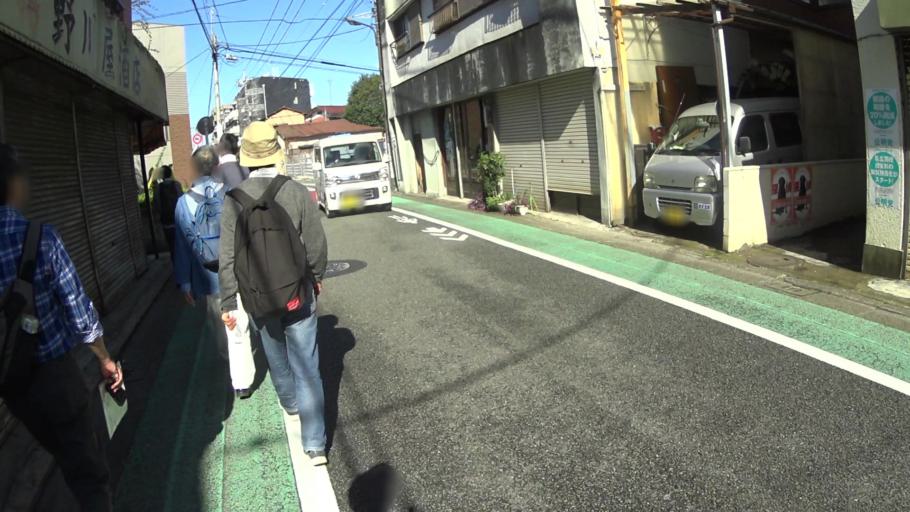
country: JP
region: Tokyo
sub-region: Machida-shi
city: Machida
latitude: 35.5511
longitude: 139.4478
